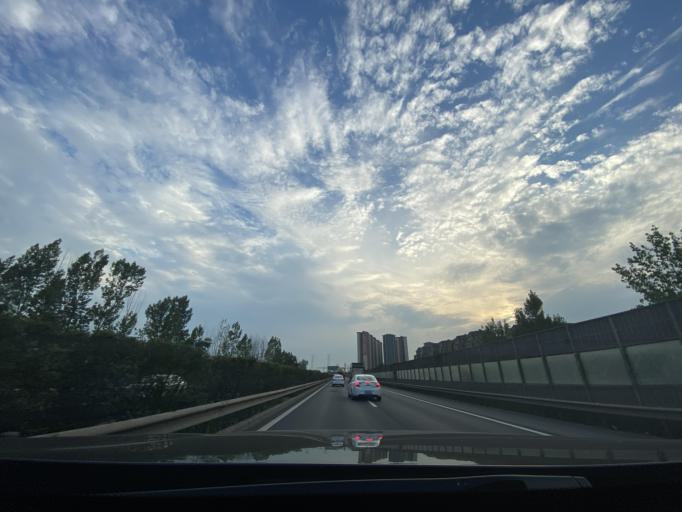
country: CN
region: Sichuan
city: Deyang
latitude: 31.0820
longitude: 104.3906
